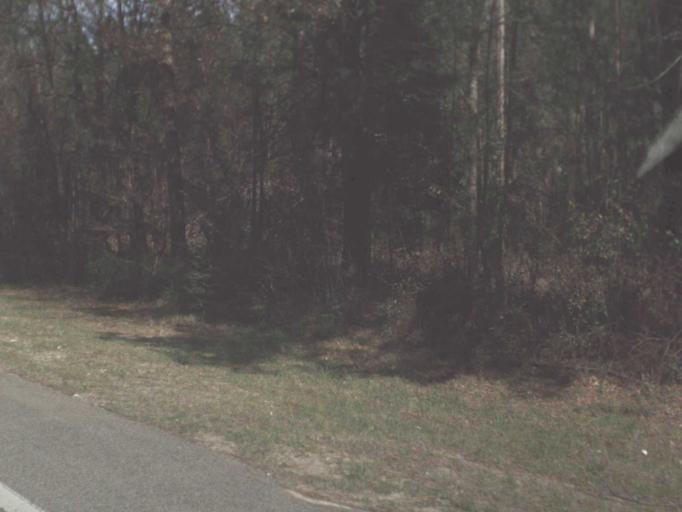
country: US
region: Florida
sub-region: Washington County
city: Chipley
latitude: 30.8378
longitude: -85.5328
